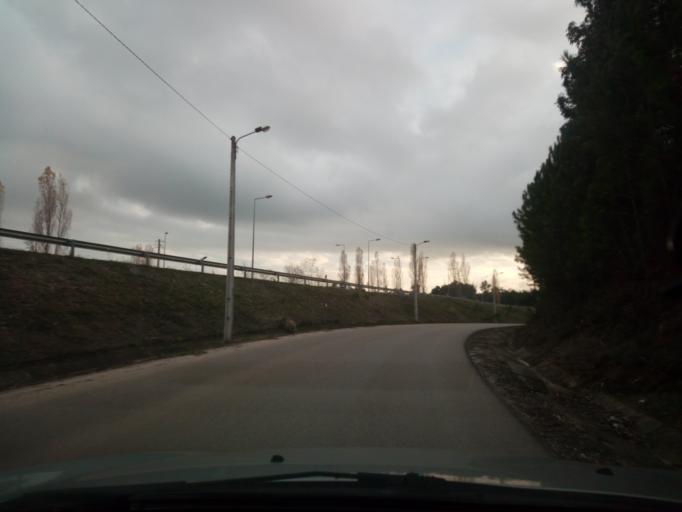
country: PT
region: Aveiro
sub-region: Agueda
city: Agueda
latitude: 40.5557
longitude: -8.4752
